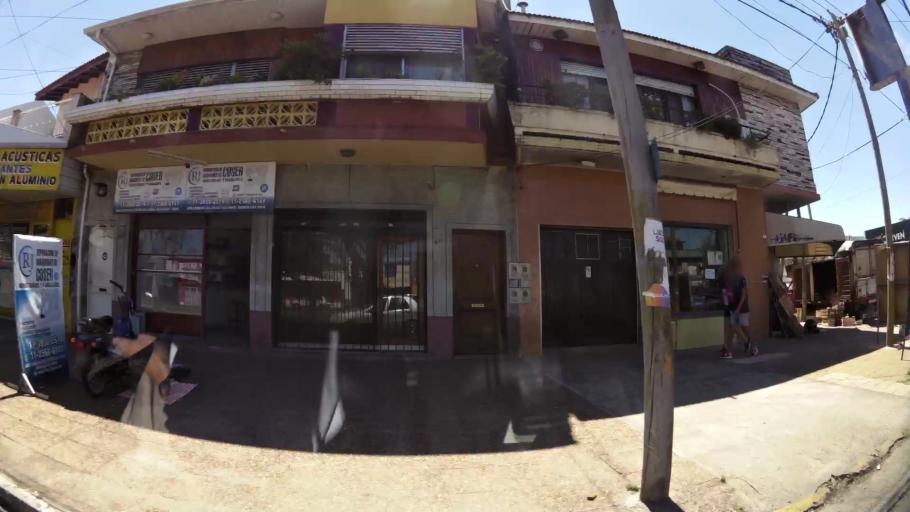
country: AR
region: Buenos Aires
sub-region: Partido de Quilmes
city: Quilmes
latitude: -34.7168
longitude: -58.2954
